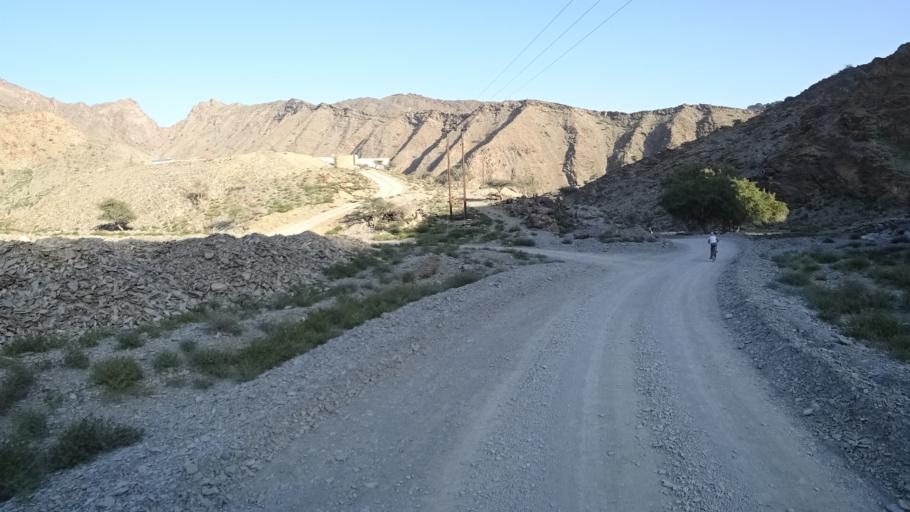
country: OM
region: Al Batinah
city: Rustaq
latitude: 23.2672
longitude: 57.3949
